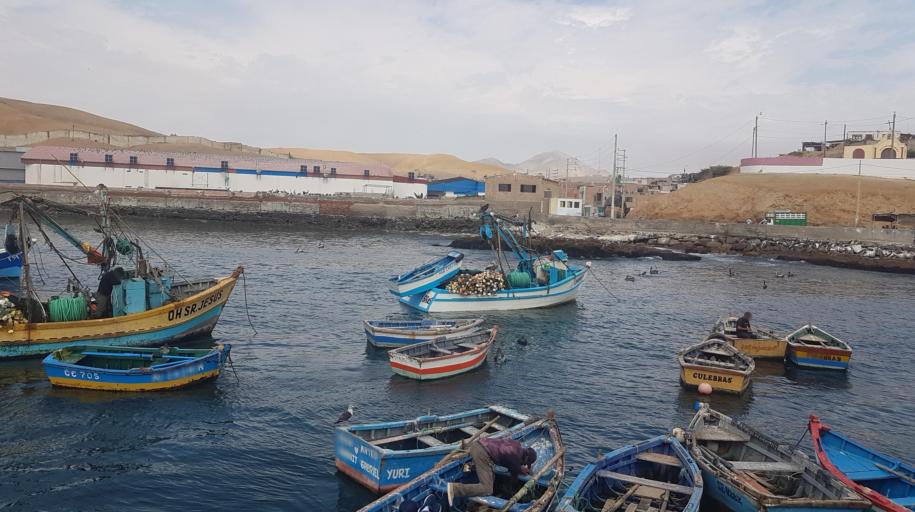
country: PE
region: Ancash
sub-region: Provincia de Huarmey
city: La Caleta Culebras
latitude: -9.9483
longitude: -78.2290
